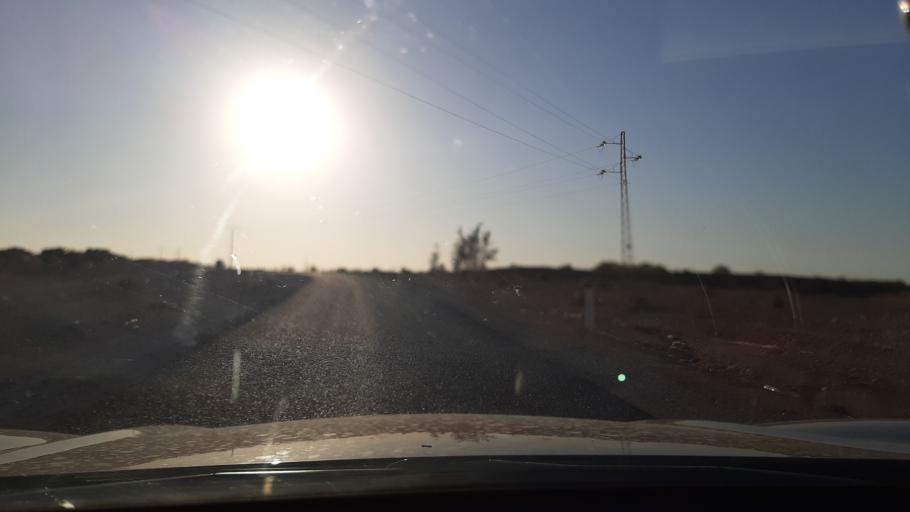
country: TN
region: Qabis
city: Matmata
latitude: 33.6170
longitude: 10.2402
